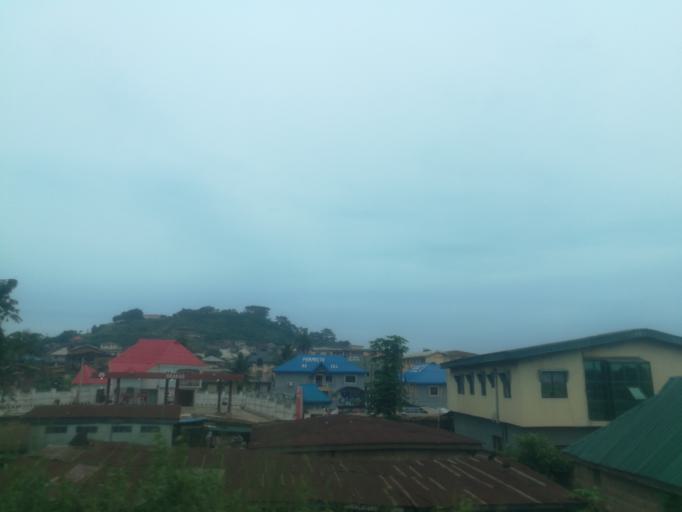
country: NG
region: Oyo
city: Egbeda
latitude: 7.3841
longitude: 3.9892
